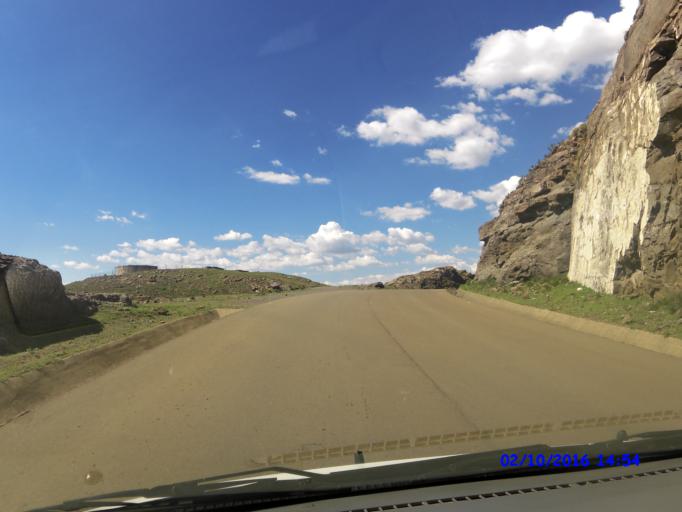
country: LS
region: Maseru
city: Nako
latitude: -29.4752
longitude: 28.0833
